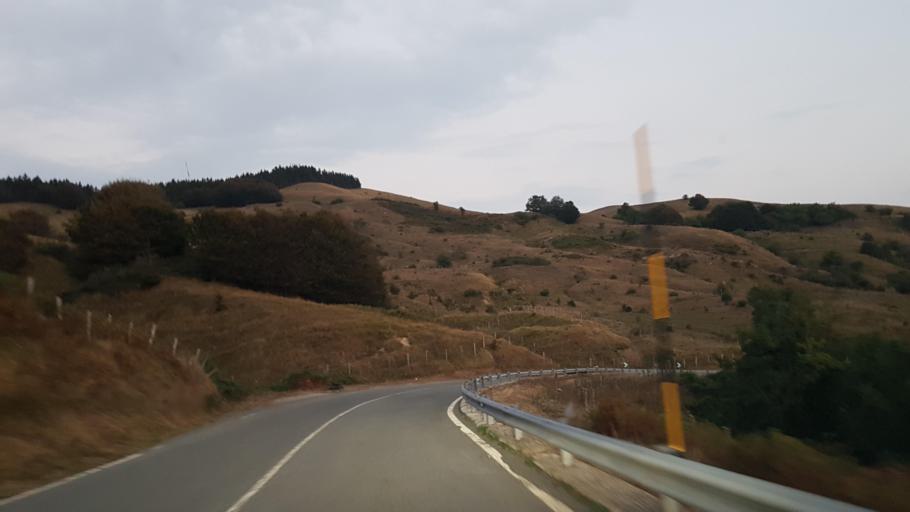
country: IT
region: Liguria
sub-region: Provincia di La Spezia
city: Varese Ligure
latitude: 44.4158
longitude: 9.6295
